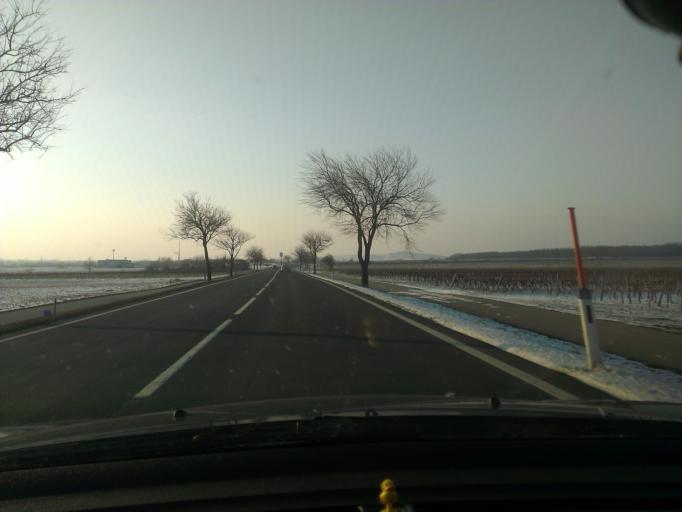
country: AT
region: Burgenland
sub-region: Eisenstadt-Umgebung
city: Donnerskirchen
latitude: 47.8836
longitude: 16.6473
